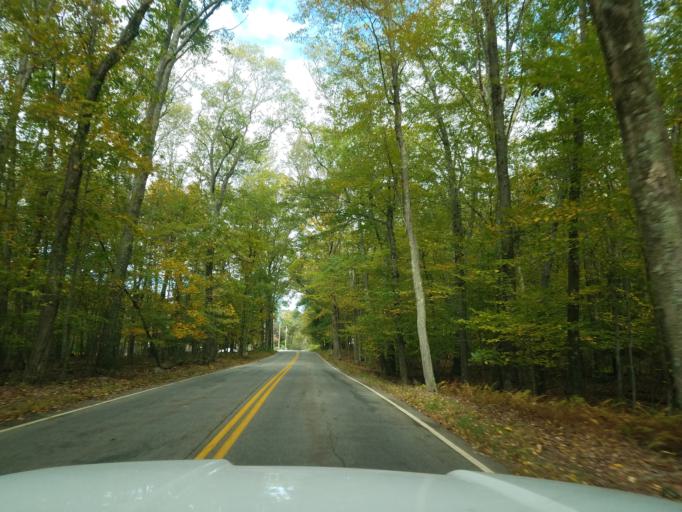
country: US
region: Connecticut
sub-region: Hartford County
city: Manchester
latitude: 41.7787
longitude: -72.4729
